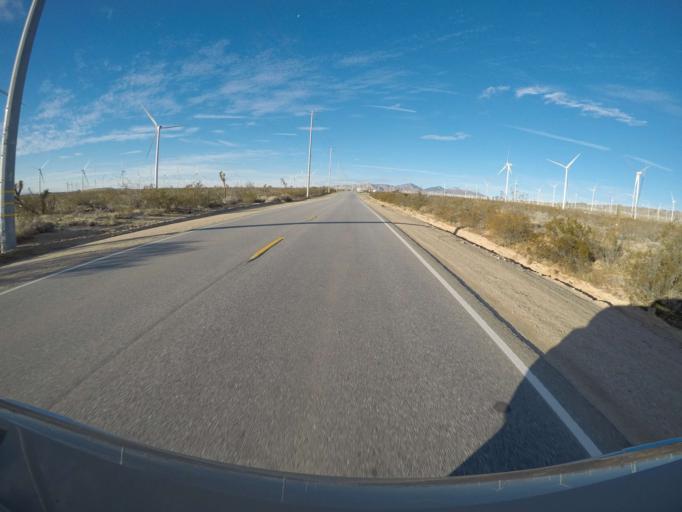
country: US
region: California
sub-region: Kern County
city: Mojave
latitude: 35.0428
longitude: -118.2302
